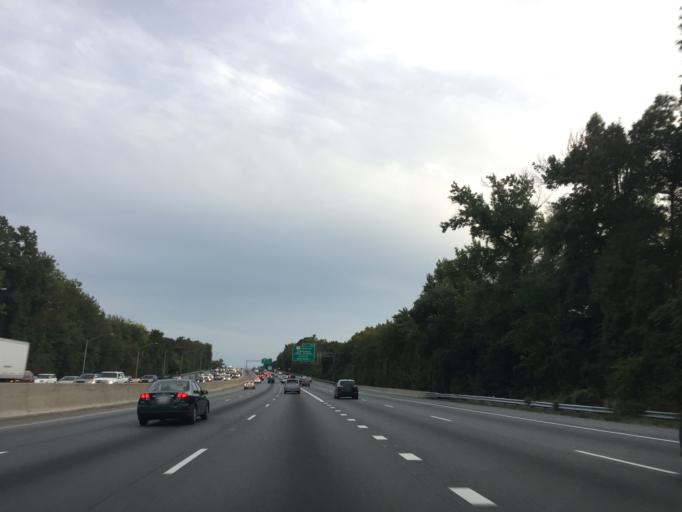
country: US
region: Maryland
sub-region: Prince George's County
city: Glenarden
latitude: 38.9259
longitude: -76.8541
